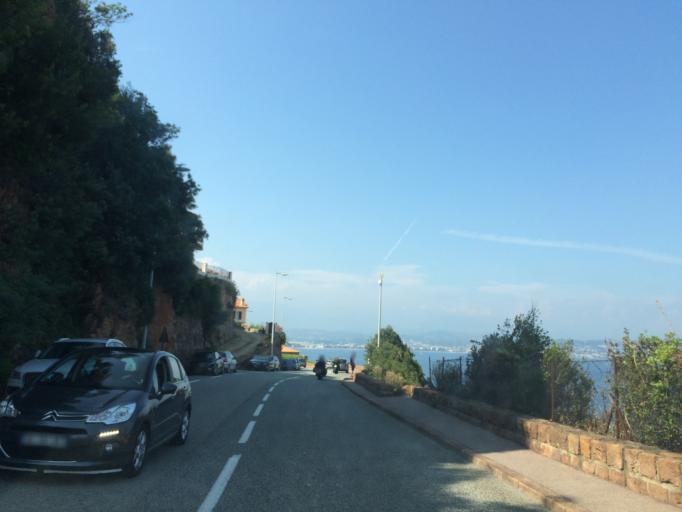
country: FR
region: Provence-Alpes-Cote d'Azur
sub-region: Departement des Alpes-Maritimes
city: Theoule-sur-Mer
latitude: 43.5032
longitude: 6.9534
